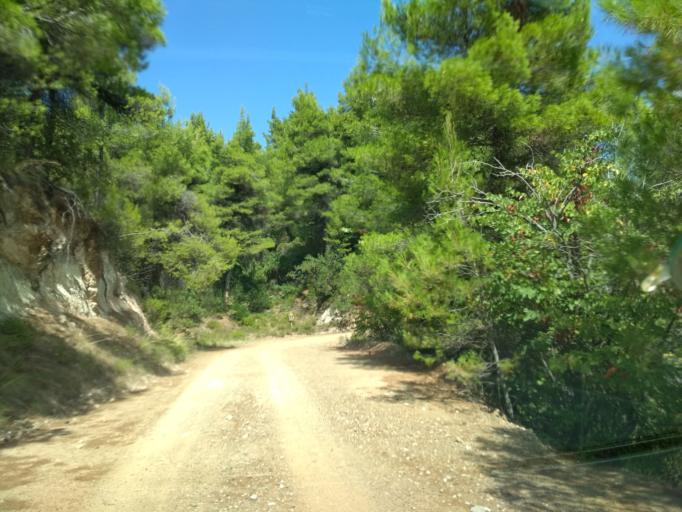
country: GR
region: Central Greece
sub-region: Nomos Evvoias
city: Roviai
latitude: 38.8401
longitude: 23.2791
